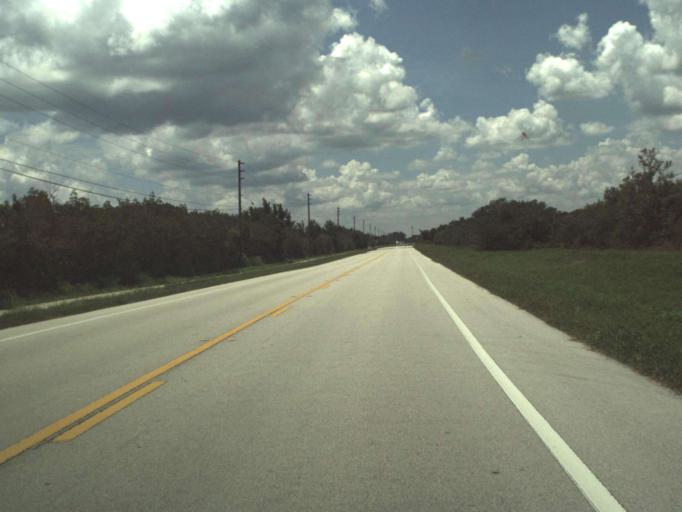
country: US
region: Florida
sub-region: Saint Lucie County
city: Fort Pierce
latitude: 27.4268
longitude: -80.2788
